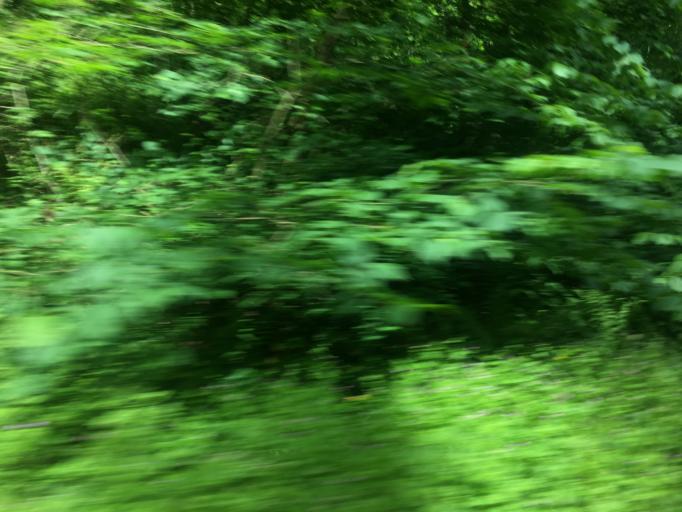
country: GB
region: Wales
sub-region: Carmarthenshire
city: Llansadwrn
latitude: 51.9938
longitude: -3.8912
